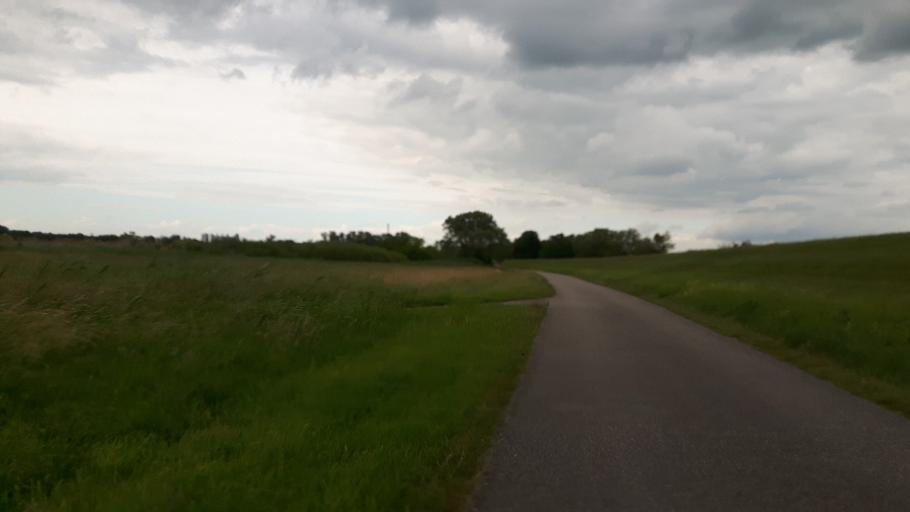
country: DE
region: Brandenburg
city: Schwedt (Oder)
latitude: 53.0645
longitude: 14.3177
